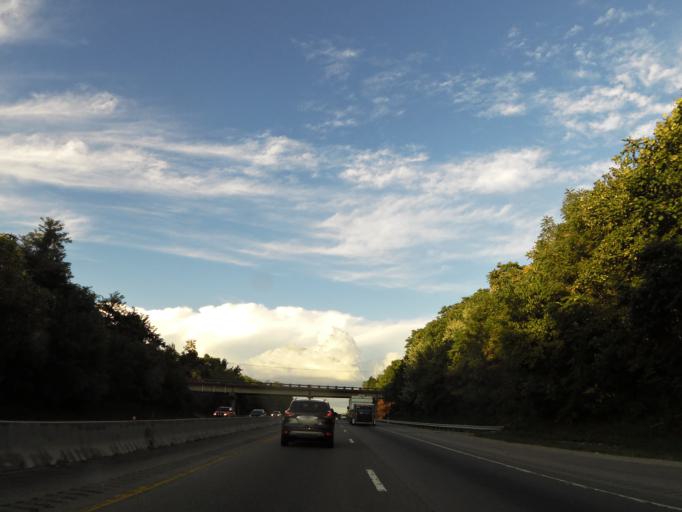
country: US
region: Tennessee
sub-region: Putnam County
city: Monterey
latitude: 36.1309
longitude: -85.3473
